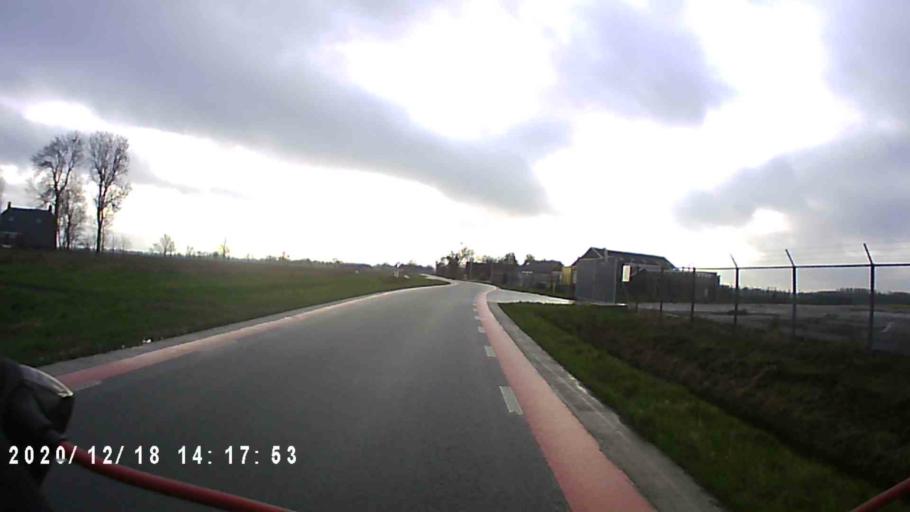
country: NL
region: Groningen
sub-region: Gemeente Bedum
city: Bedum
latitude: 53.2606
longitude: 6.6453
